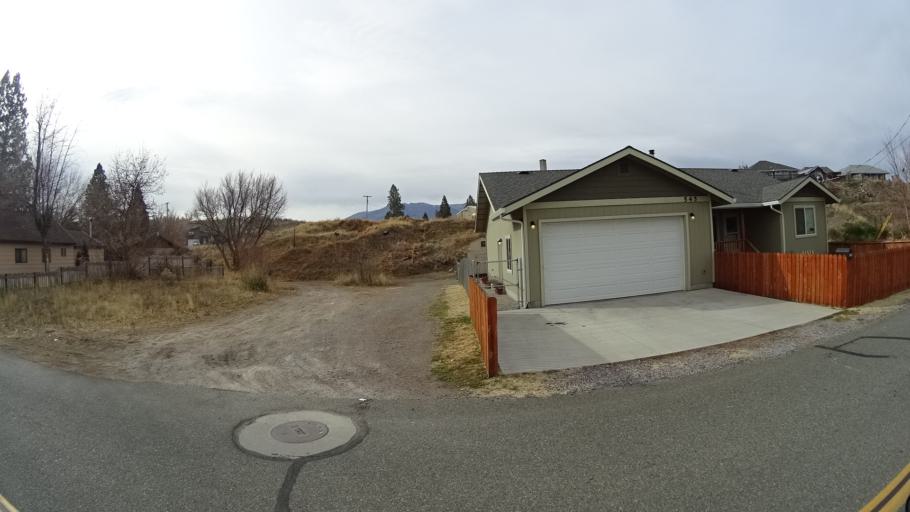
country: US
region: California
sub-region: Siskiyou County
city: Weed
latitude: 41.4297
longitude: -122.3775
